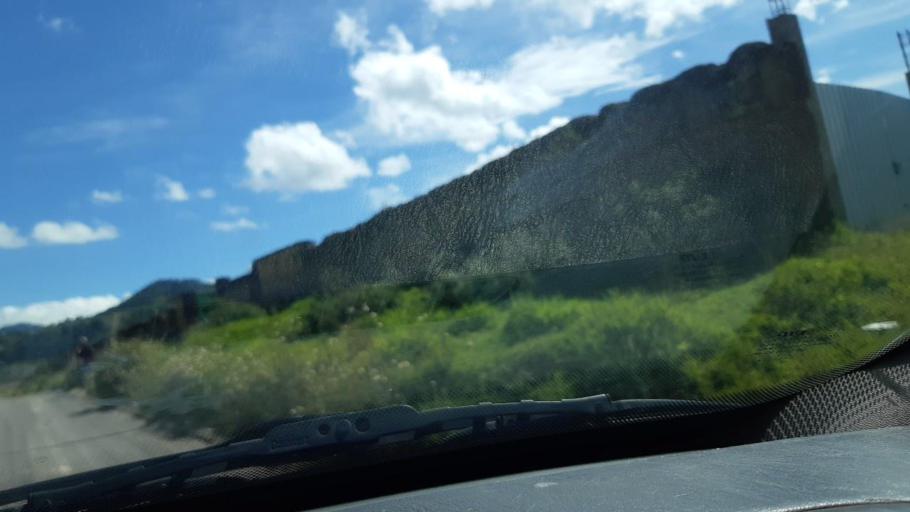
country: GT
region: Quetzaltenango
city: Salcaja
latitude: 14.8863
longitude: -91.4429
